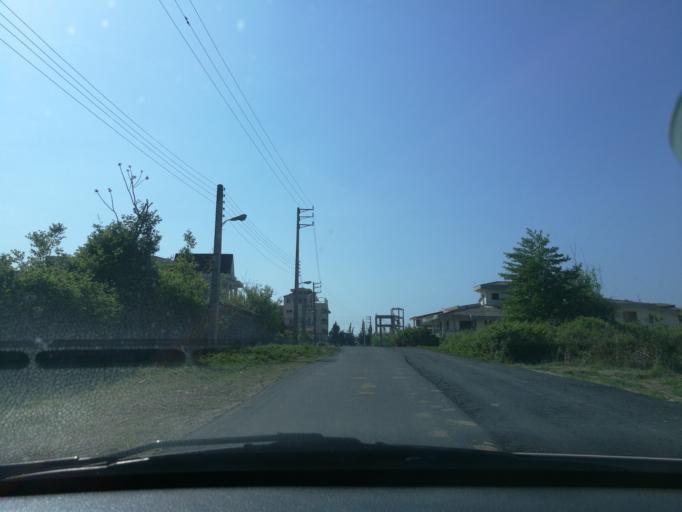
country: IR
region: Mazandaran
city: Chalus
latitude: 36.6725
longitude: 51.4320
